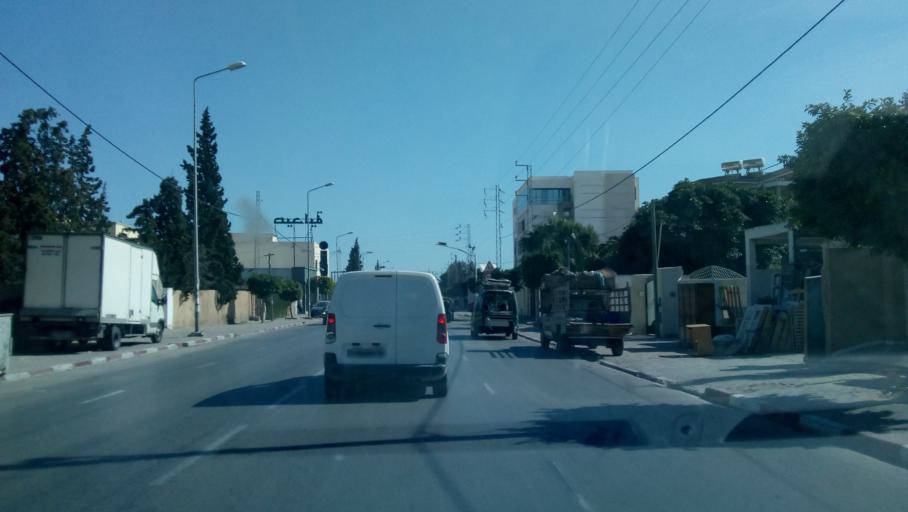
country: TN
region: Safaqis
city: Sfax
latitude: 34.7712
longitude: 10.7321
